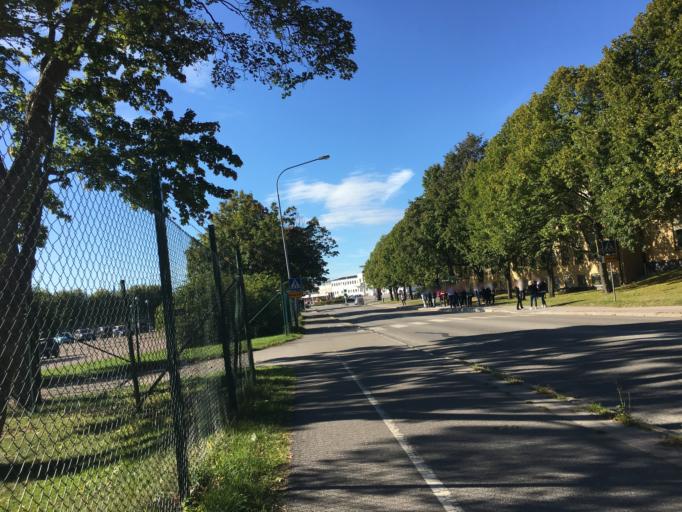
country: SE
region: Uppsala
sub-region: Uppsala Kommun
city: Uppsala
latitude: 59.8554
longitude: 17.6676
